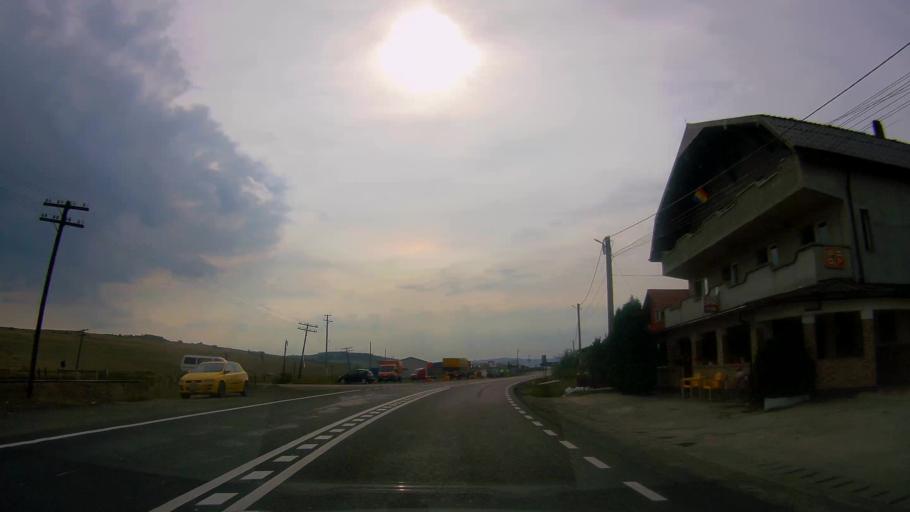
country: RO
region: Salaj
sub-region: Comuna Hereclean
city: Hereclean
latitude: 47.2549
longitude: 22.9785
